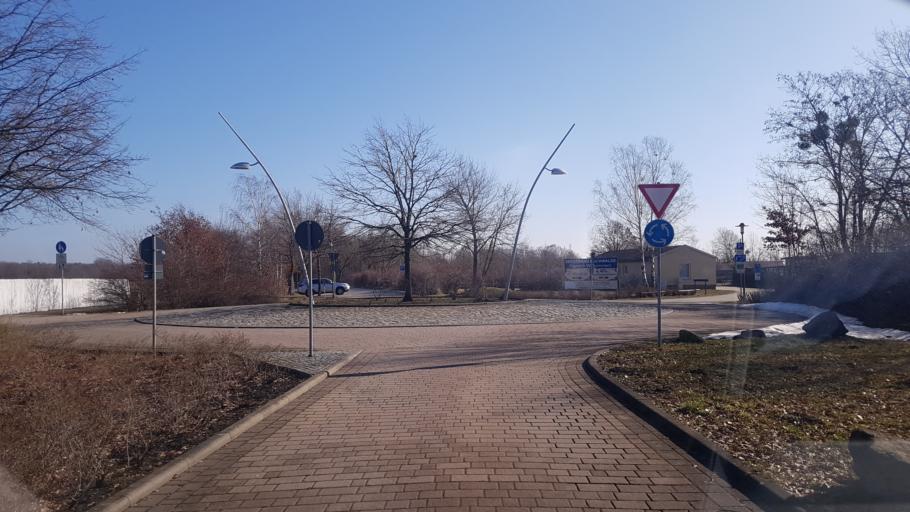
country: DE
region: Brandenburg
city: Senftenberg
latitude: 51.5125
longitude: 14.0240
